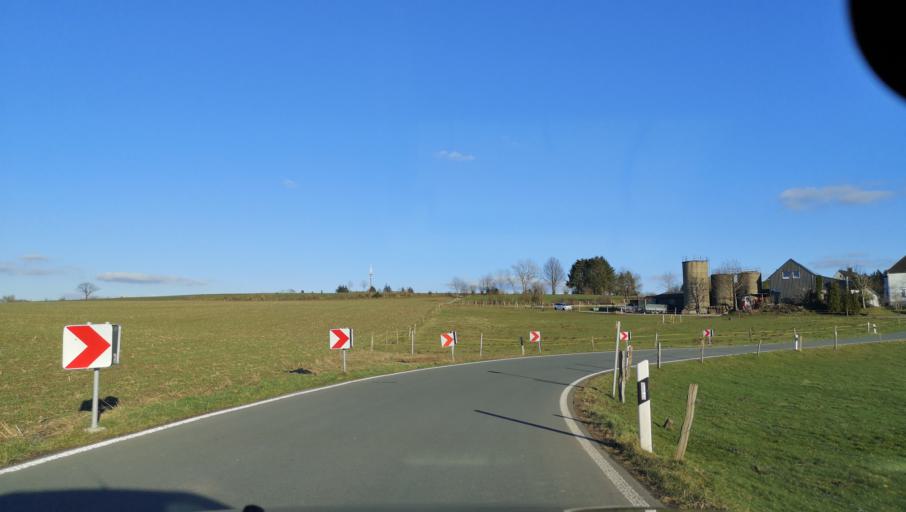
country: DE
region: North Rhine-Westphalia
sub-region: Regierungsbezirk Arnsberg
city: Breckerfeld
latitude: 51.2467
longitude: 7.4540
